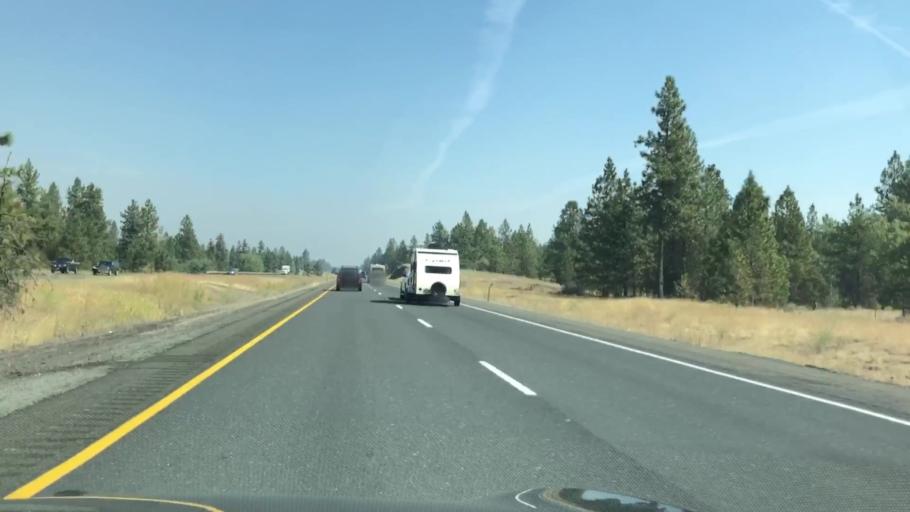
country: US
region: Washington
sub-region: Spokane County
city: Medical Lake
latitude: 47.4558
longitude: -117.7653
